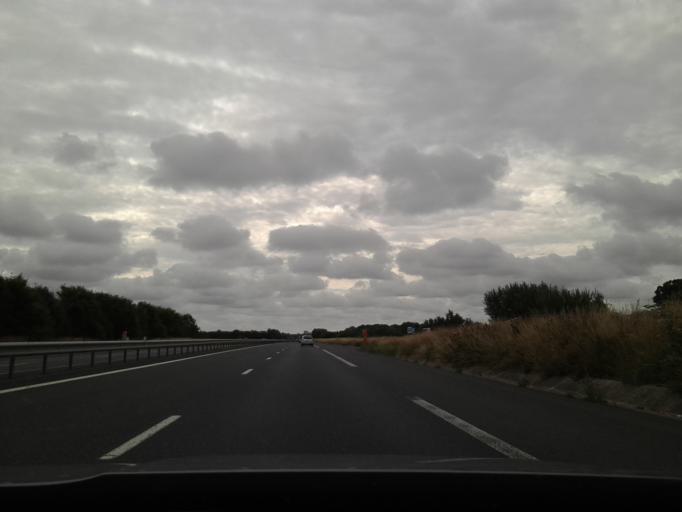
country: FR
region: Lower Normandy
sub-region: Departement du Calvados
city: Port-en-Bessin-Huppain
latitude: 49.2917
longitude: -0.7736
